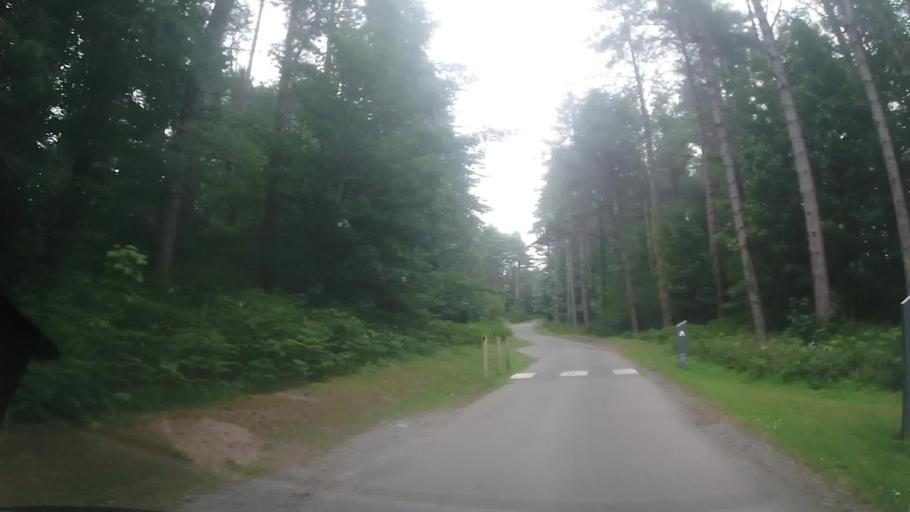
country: GB
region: Wales
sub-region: Gwynedd
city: Caernarfon
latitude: 53.1563
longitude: -4.3744
